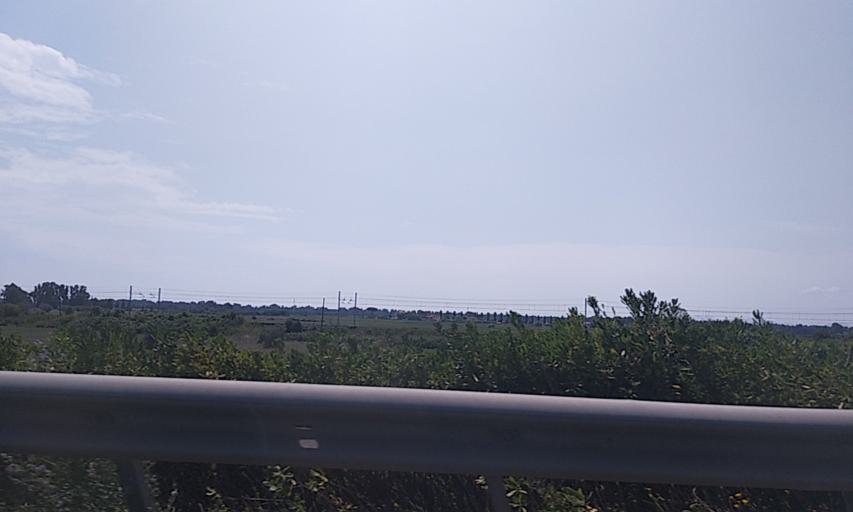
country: IT
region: Tuscany
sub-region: Provincia di Livorno
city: Riotorto
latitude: 42.9737
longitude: 10.6599
